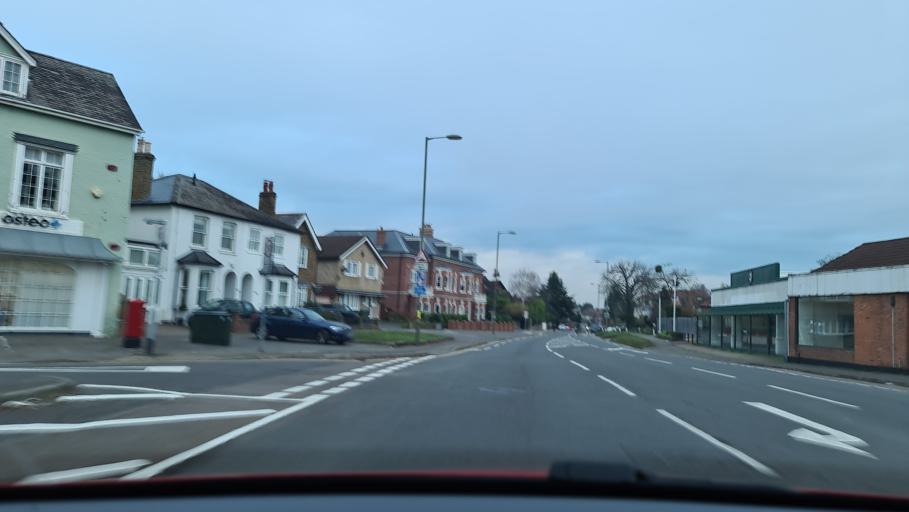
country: GB
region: England
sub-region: Surrey
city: Thames Ditton
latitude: 51.3867
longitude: -0.3300
